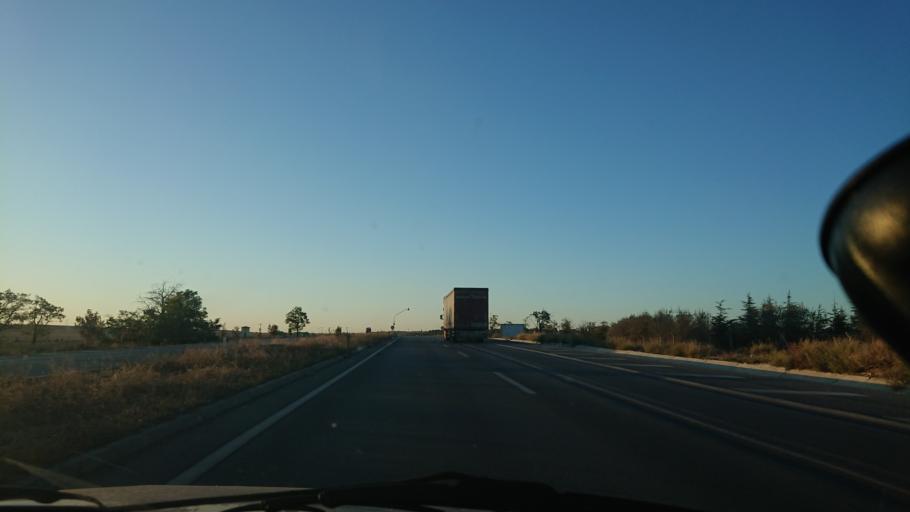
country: TR
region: Eskisehir
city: Mahmudiye
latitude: 39.4844
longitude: 30.9859
